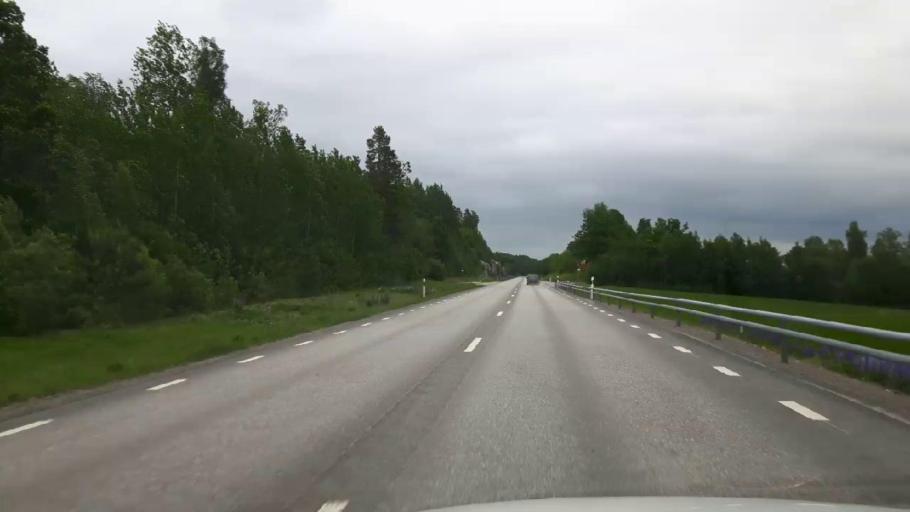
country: SE
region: Vaestmanland
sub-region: Kopings Kommun
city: Kolsva
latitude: 59.5678
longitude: 15.8815
